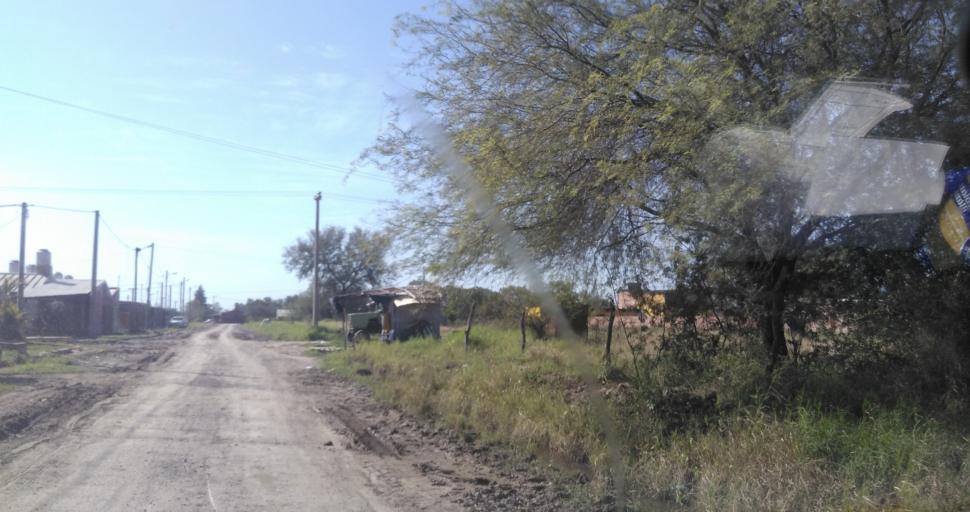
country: AR
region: Chaco
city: Fontana
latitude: -27.4574
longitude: -59.0484
